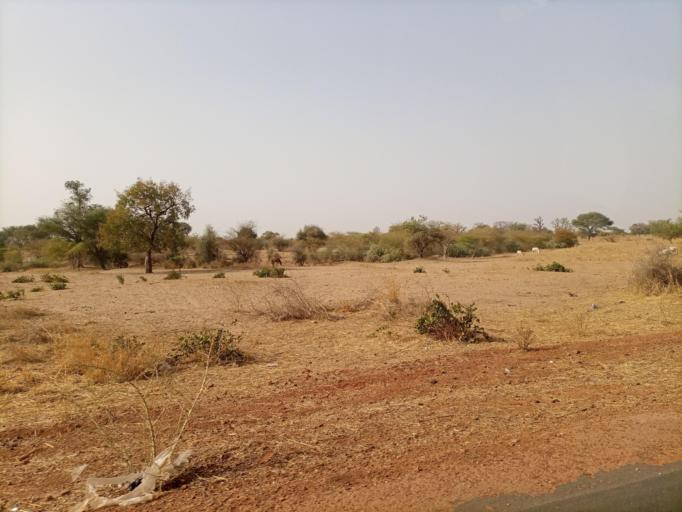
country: SN
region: Fatick
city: Foundiougne
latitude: 14.1247
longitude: -16.4233
